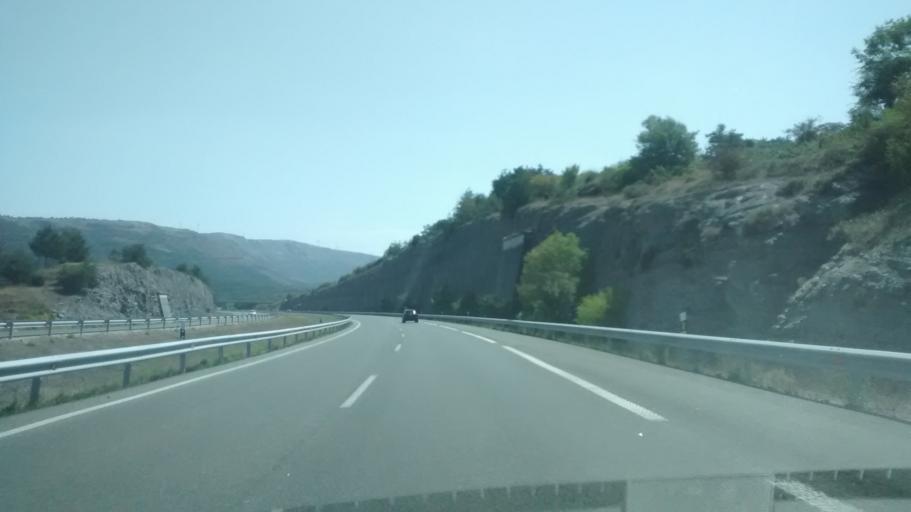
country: ES
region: Basque Country
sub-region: Provincia de Alava
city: Murguia
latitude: 42.9165
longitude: -2.9036
